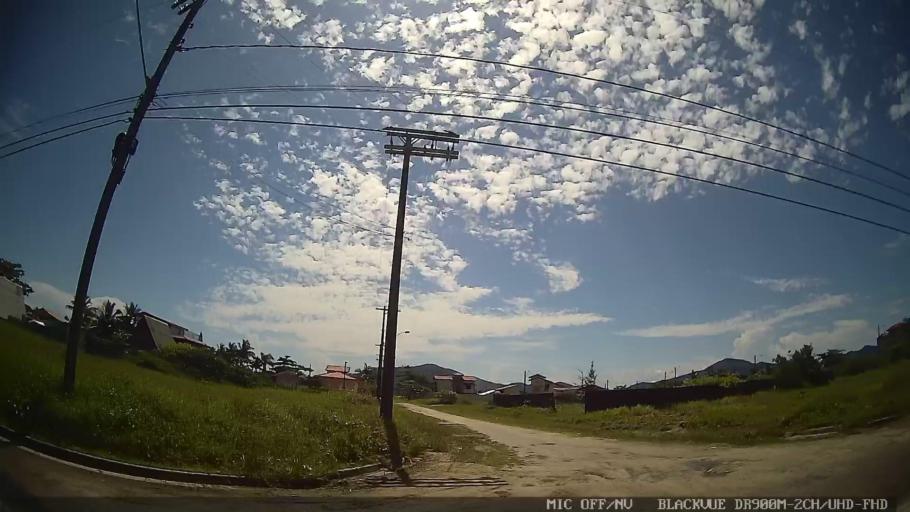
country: BR
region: Sao Paulo
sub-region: Iguape
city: Iguape
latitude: -24.7310
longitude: -47.5191
